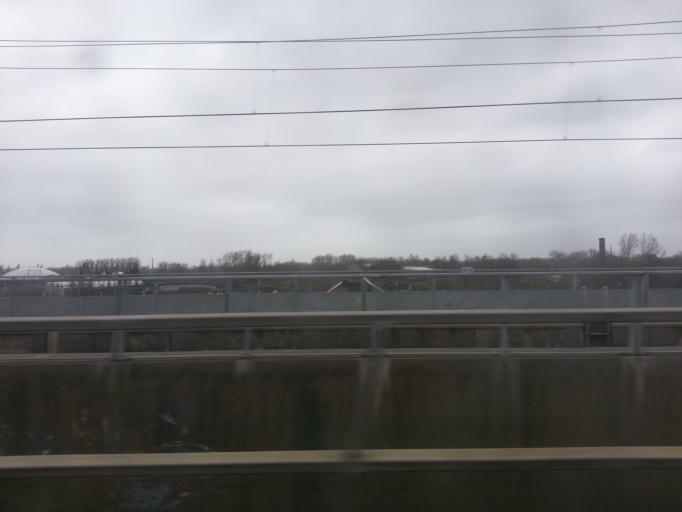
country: NL
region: South Holland
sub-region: Gemeente Rotterdam
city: Delfshaven
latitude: 51.9232
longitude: 4.4513
